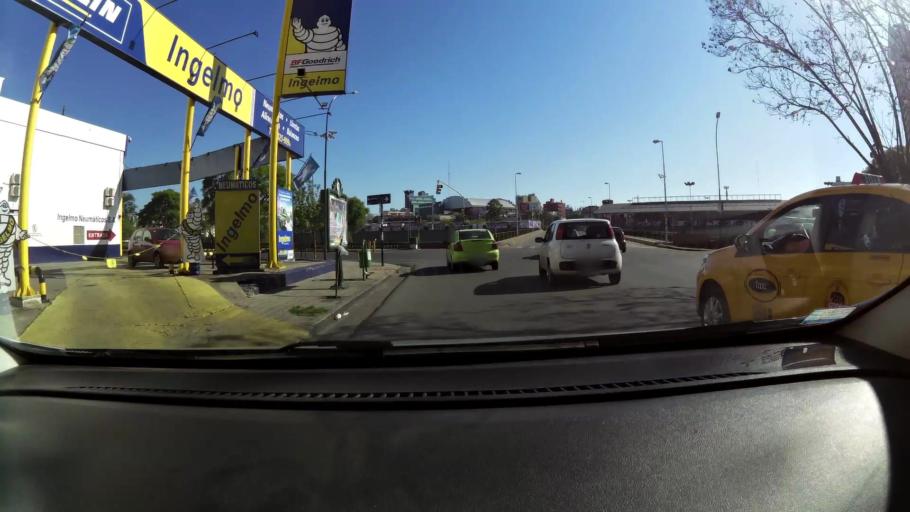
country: AR
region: Cordoba
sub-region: Departamento de Capital
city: Cordoba
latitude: -31.4084
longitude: -64.1765
